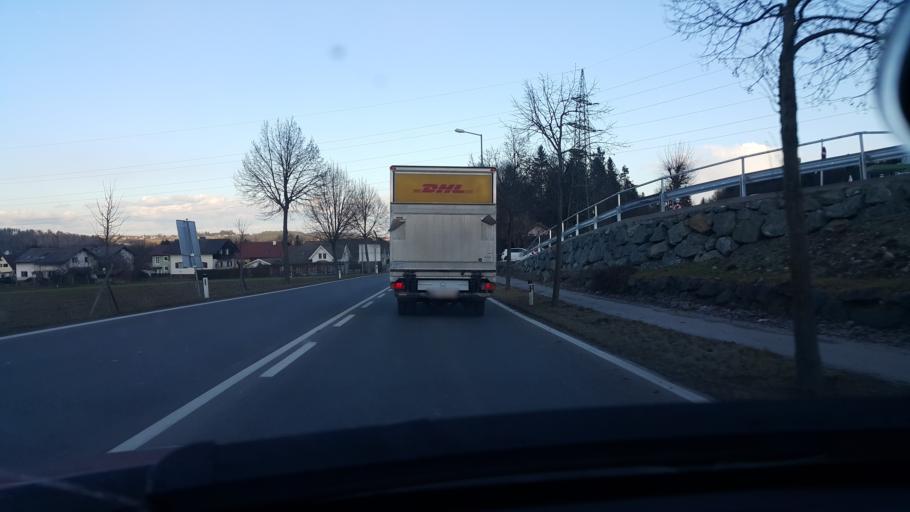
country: AT
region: Styria
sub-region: Politischer Bezirk Deutschlandsberg
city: Deutschlandsberg
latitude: 46.8124
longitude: 15.2290
